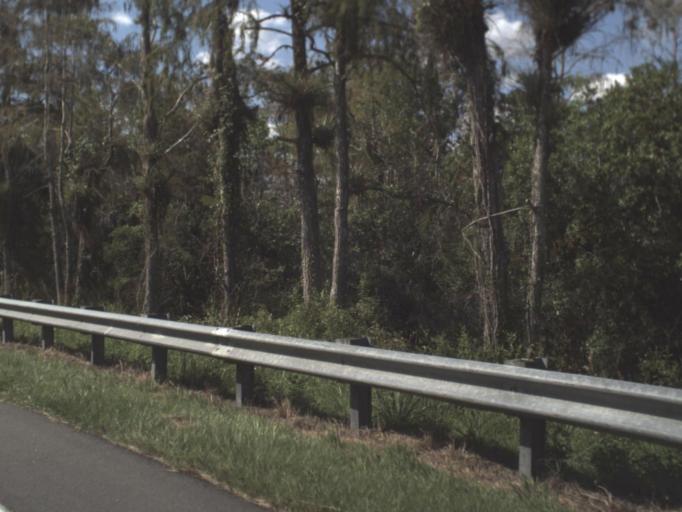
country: US
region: Florida
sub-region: Miami-Dade County
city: Kendall West
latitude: 25.8498
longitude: -80.9633
